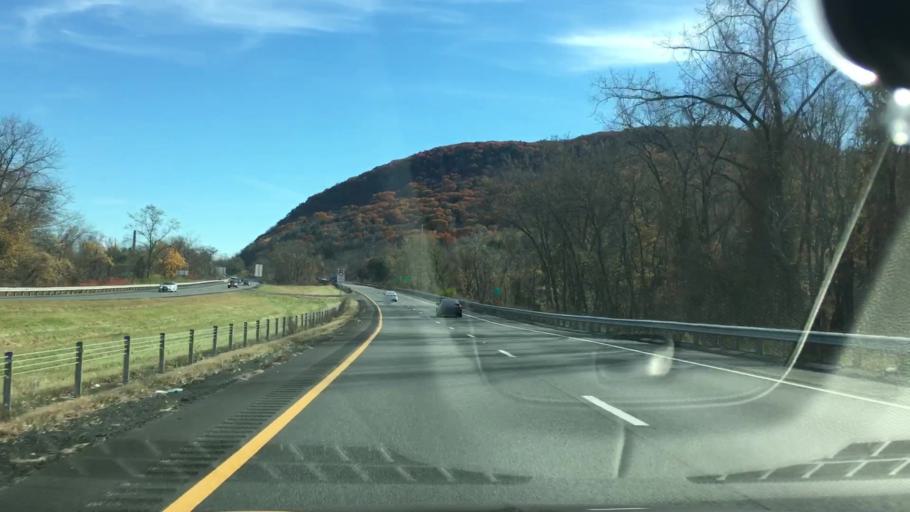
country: US
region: Massachusetts
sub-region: Hampshire County
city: Northampton
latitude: 42.2896
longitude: -72.6258
